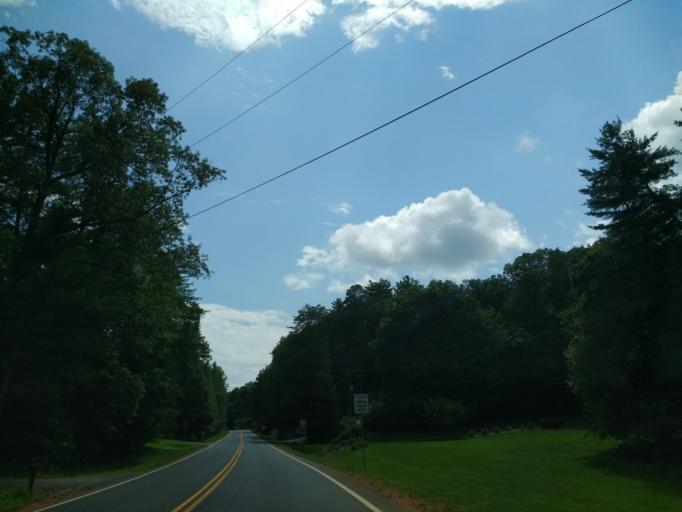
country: US
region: Georgia
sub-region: White County
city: Cleveland
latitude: 34.7087
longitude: -83.7534
